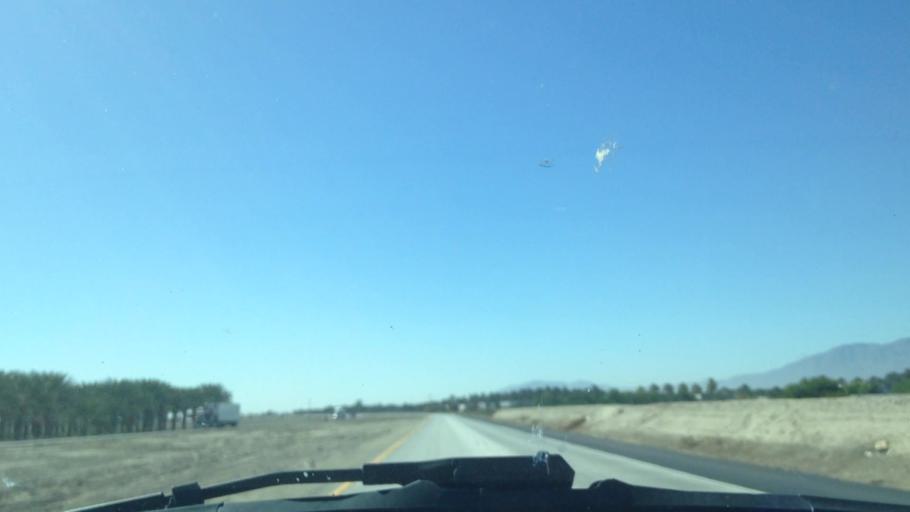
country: US
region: California
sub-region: Riverside County
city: Thermal
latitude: 33.6260
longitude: -116.1221
